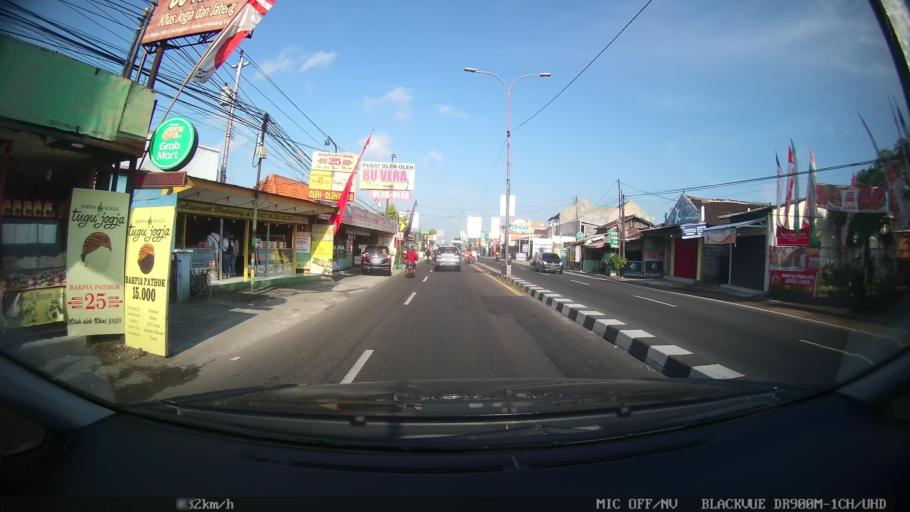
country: ID
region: Daerah Istimewa Yogyakarta
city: Gamping Lor
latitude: -7.8013
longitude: 110.3225
